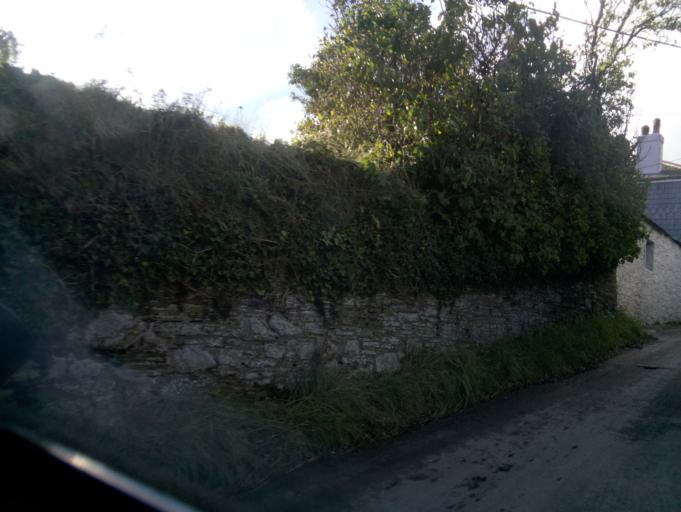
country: GB
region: England
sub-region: Devon
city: Totnes
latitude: 50.3623
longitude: -3.7360
